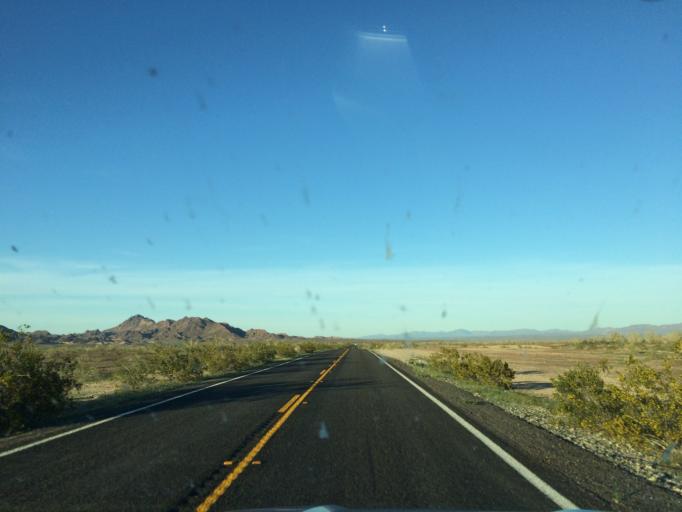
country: US
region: California
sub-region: Riverside County
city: Mesa Verde
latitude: 33.2580
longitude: -114.8089
